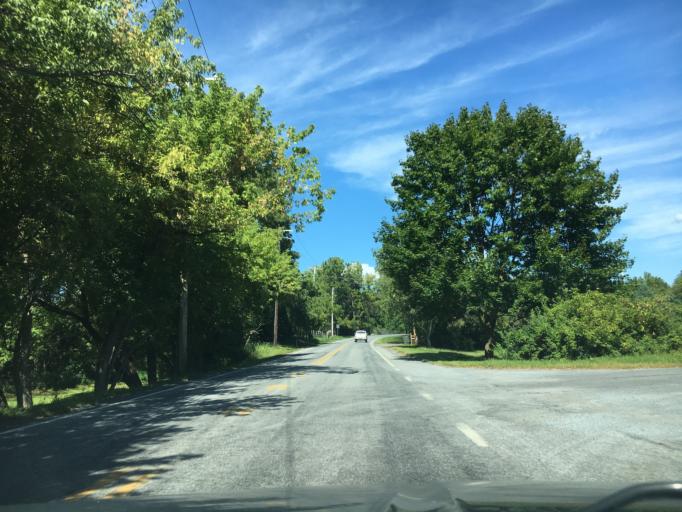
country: US
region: Pennsylvania
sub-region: Berks County
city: Topton
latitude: 40.5203
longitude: -75.6893
